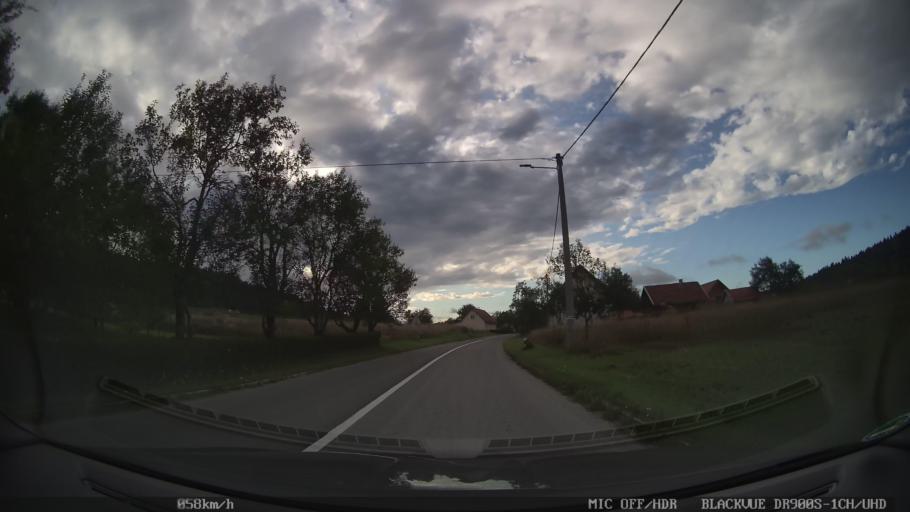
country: HR
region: Licko-Senjska
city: Jezerce
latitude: 44.9714
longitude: 15.5036
